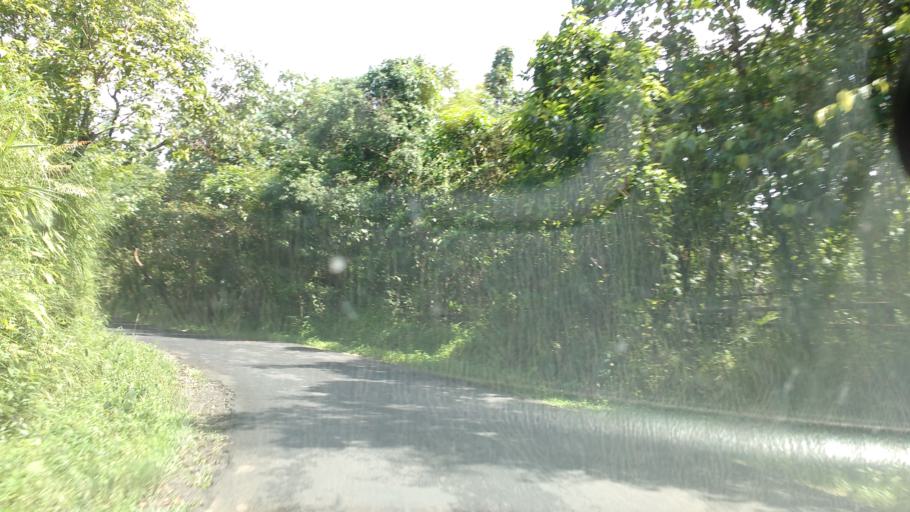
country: IN
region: Meghalaya
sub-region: East Khasi Hills
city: Cherrapunji
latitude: 25.2178
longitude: 91.9223
